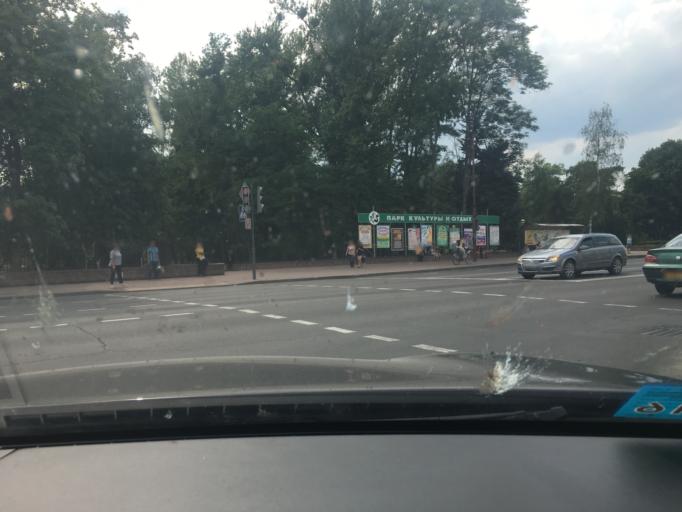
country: BY
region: Brest
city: Brest
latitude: 52.0958
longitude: 23.6828
